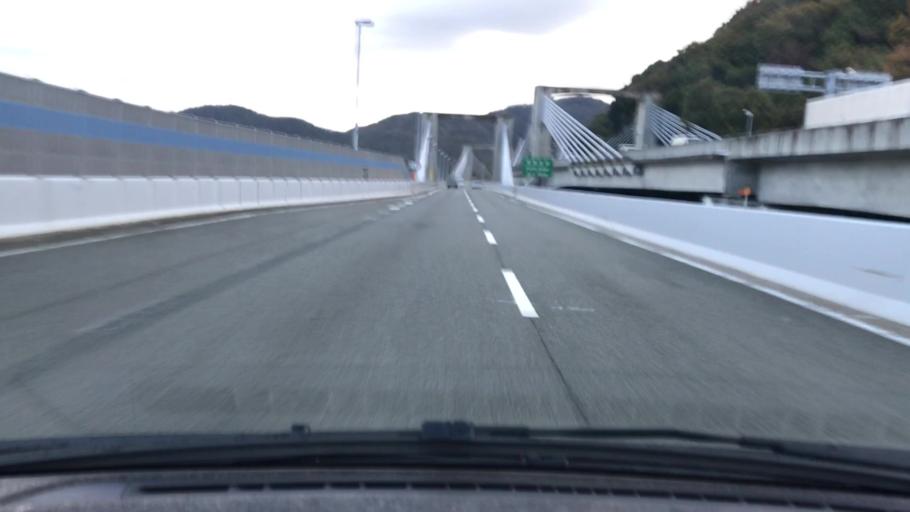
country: JP
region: Hyogo
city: Sandacho
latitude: 34.7861
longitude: 135.2184
